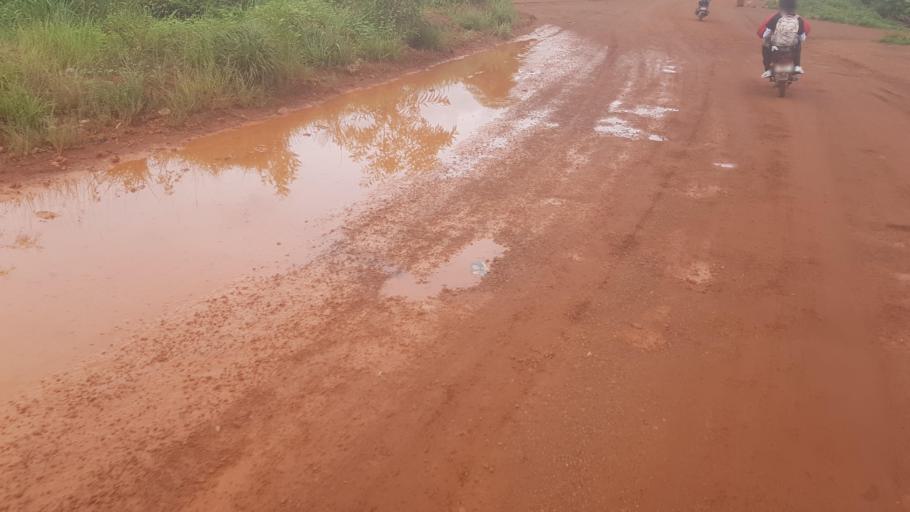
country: SL
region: Southern Province
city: Mogbwemo
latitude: 7.7657
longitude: -12.3024
